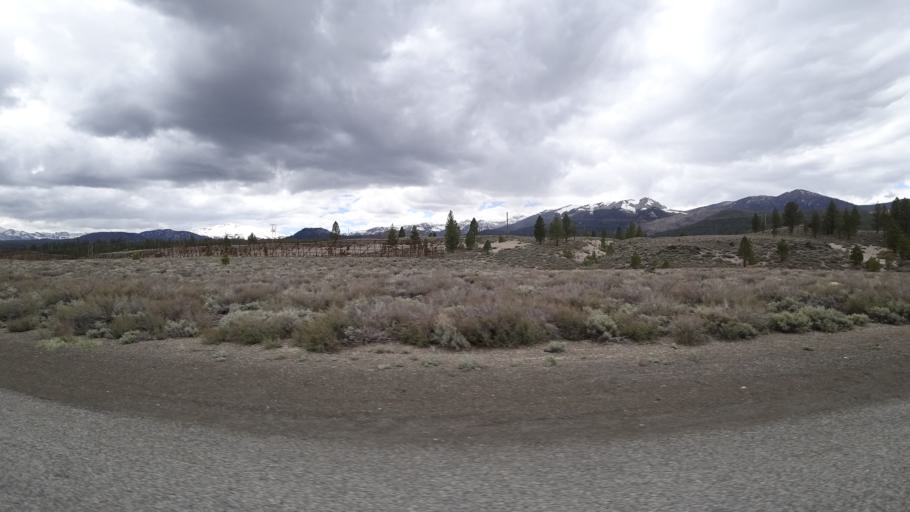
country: US
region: California
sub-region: Mono County
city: Mammoth Lakes
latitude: 37.7409
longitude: -118.9751
